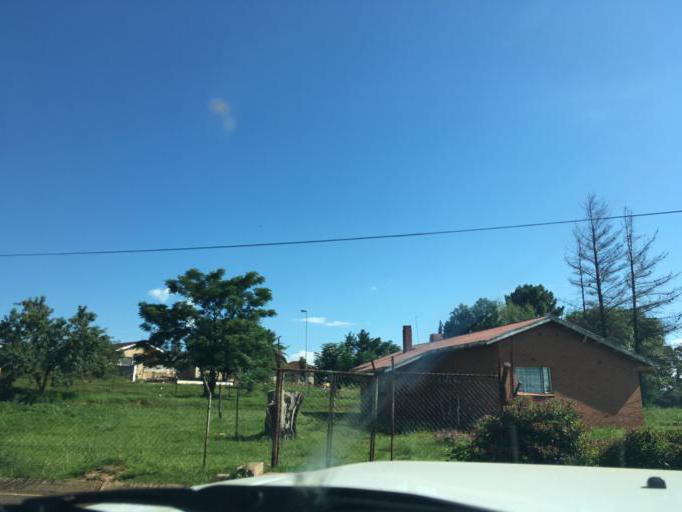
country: LS
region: Leribe
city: Leribe
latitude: -28.8678
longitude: 28.0477
